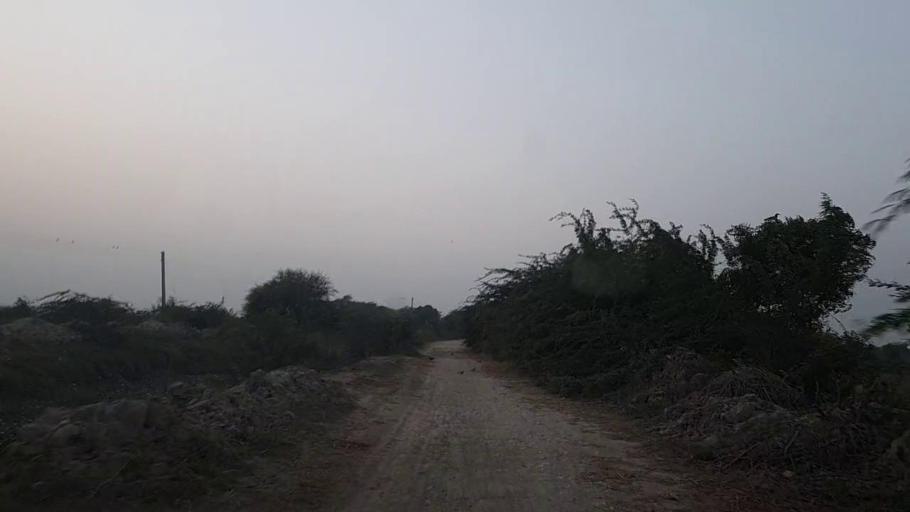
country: PK
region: Sindh
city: Mirpur Sakro
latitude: 24.5750
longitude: 67.7878
